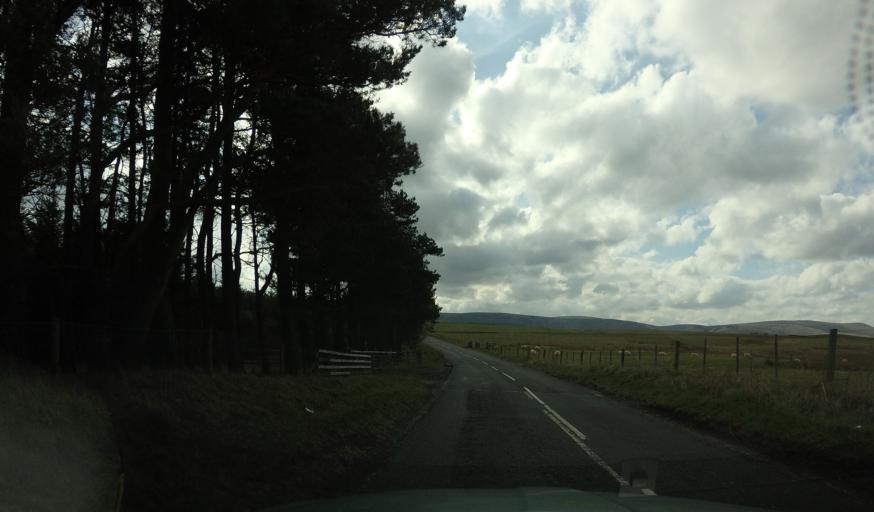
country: GB
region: Scotland
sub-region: Midlothian
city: Bonnyrigg
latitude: 55.7924
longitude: -3.1388
